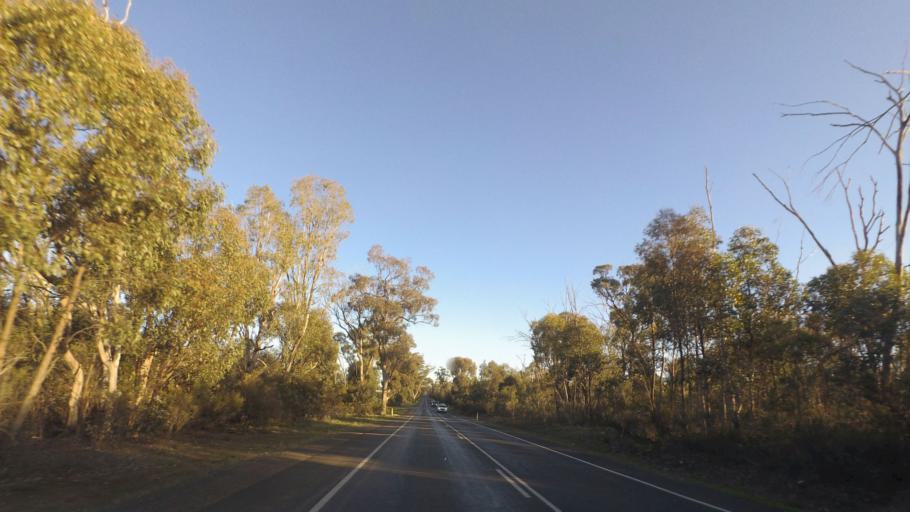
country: AU
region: Victoria
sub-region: Mount Alexander
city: Castlemaine
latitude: -37.0682
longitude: 144.5117
